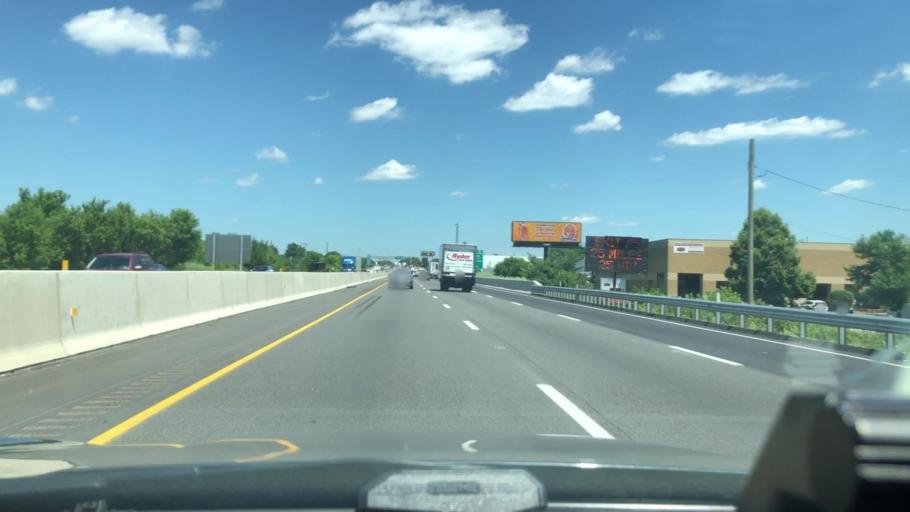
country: US
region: Pennsylvania
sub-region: Lehigh County
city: Trexlertown
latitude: 40.5819
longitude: -75.6133
